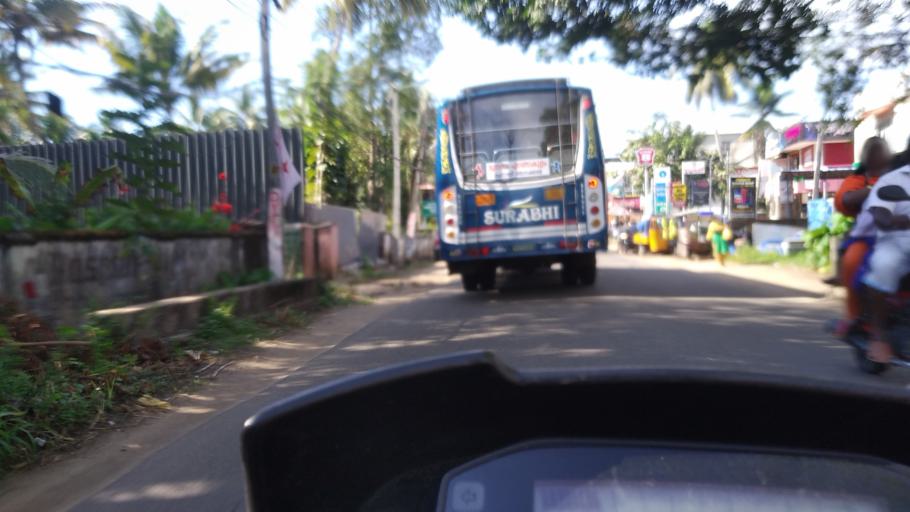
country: IN
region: Kerala
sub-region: Ernakulam
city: Elur
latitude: 10.0410
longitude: 76.2190
